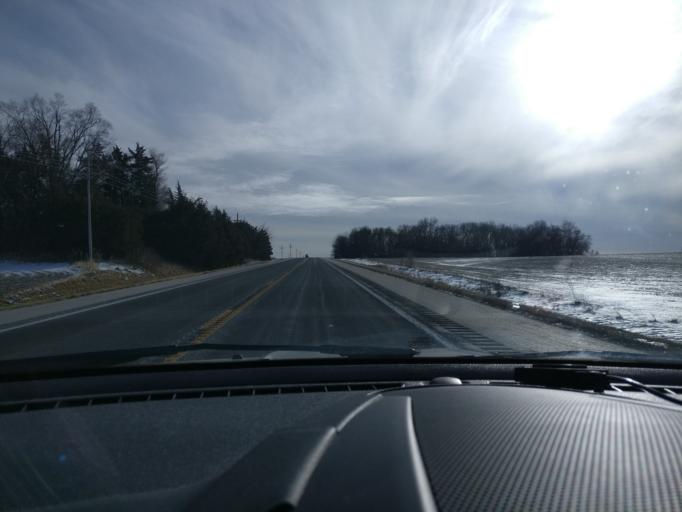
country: US
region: Nebraska
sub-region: Dodge County
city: Fremont
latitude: 41.3703
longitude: -96.5018
